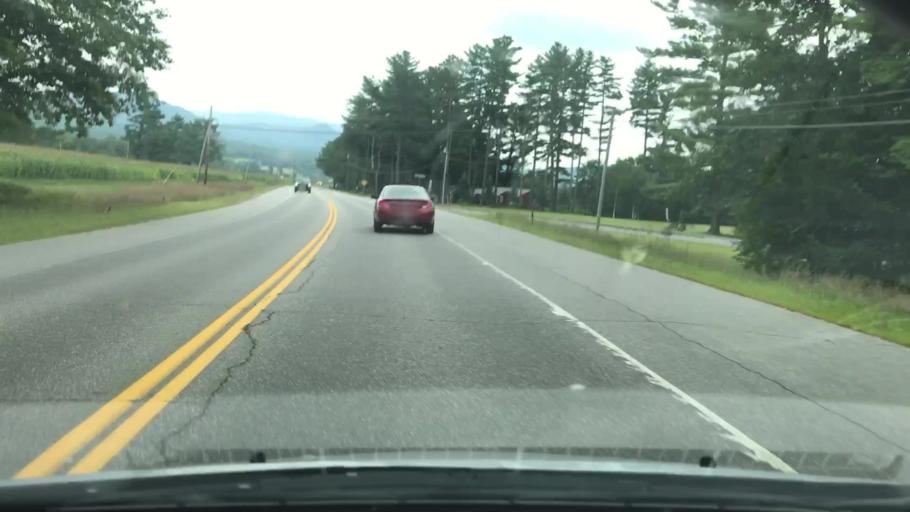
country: US
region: New Hampshire
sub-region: Grafton County
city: North Haverhill
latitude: 44.1064
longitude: -72.0362
